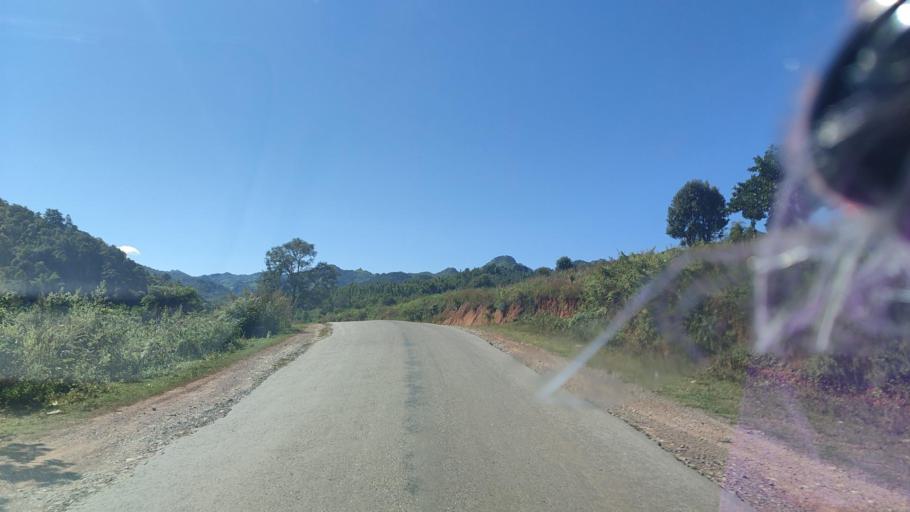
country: MM
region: Shan
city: Taunggyi
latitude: 20.8900
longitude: 97.5475
